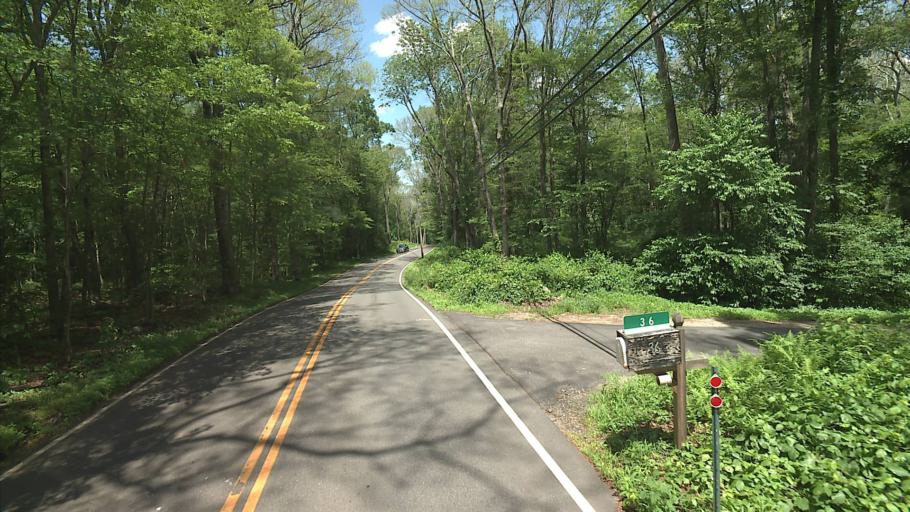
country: US
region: Connecticut
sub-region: New London County
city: Colchester
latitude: 41.4896
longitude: -72.3535
